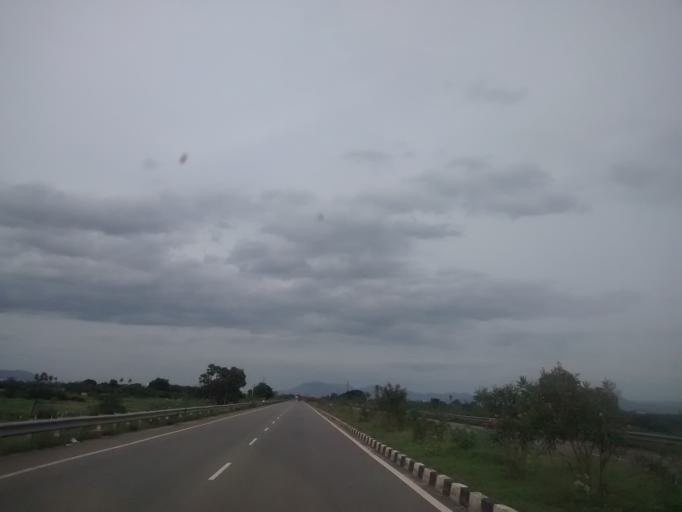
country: IN
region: Andhra Pradesh
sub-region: Chittoor
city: Narasingapuram
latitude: 13.6034
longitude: 79.3729
